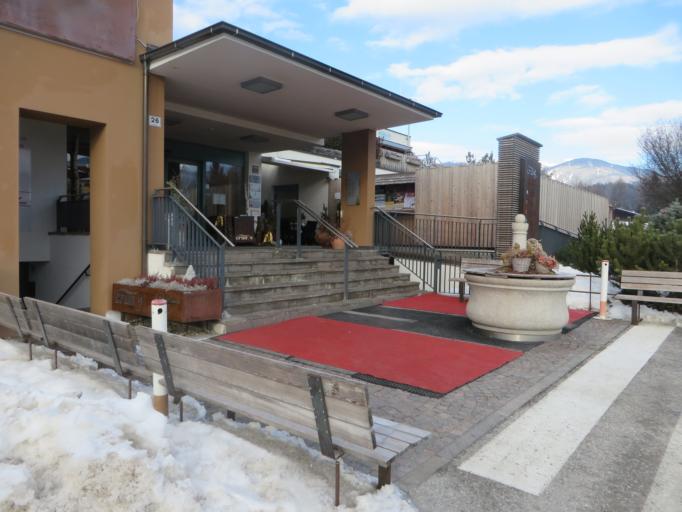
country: IT
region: Trentino-Alto Adige
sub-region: Bolzano
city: Riscone
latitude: 46.7795
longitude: 11.9378
